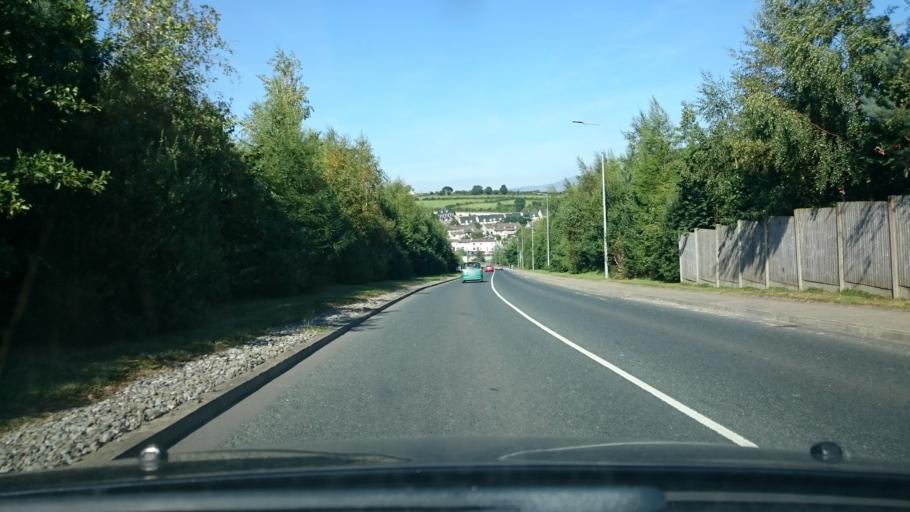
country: IE
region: Leinster
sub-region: Kilkenny
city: Graiguenamanagh
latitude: 52.5419
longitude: -6.9626
